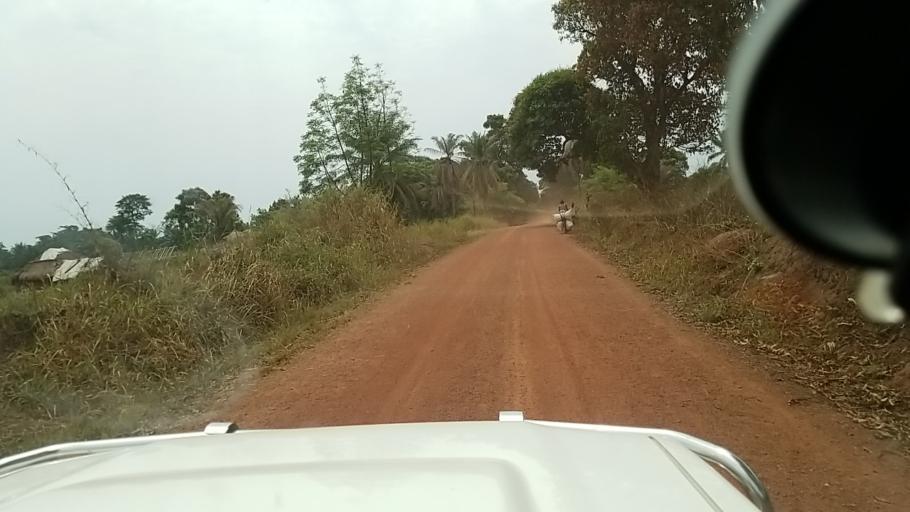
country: CD
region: Equateur
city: Libenge
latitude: 3.7334
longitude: 18.7764
